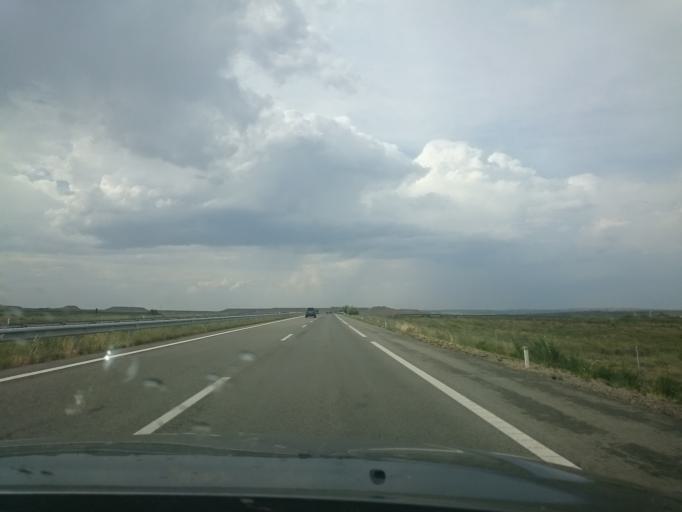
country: ES
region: La Rioja
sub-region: Provincia de La Rioja
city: Rincon de Soto
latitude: 42.1798
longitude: -1.8377
